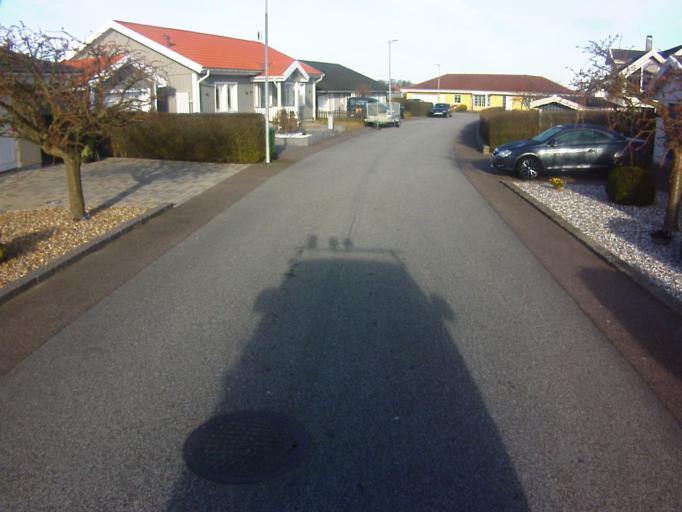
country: SE
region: Skane
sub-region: Kavlinge Kommun
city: Kaevlinge
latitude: 55.7955
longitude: 13.0906
